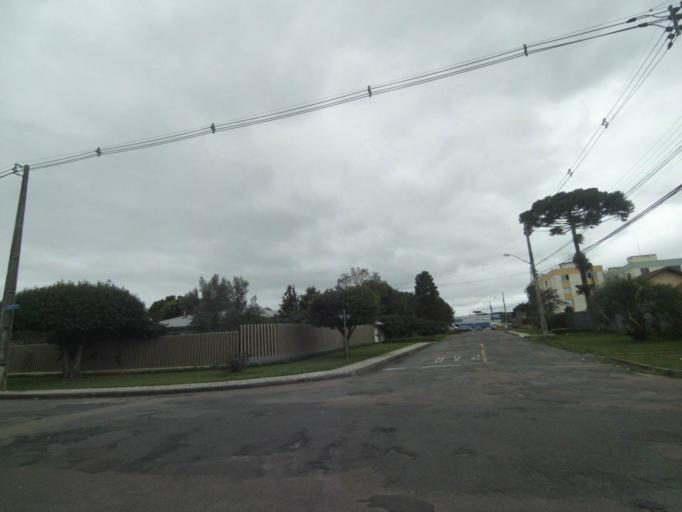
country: BR
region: Parana
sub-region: Curitiba
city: Curitiba
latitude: -25.4935
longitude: -49.2969
